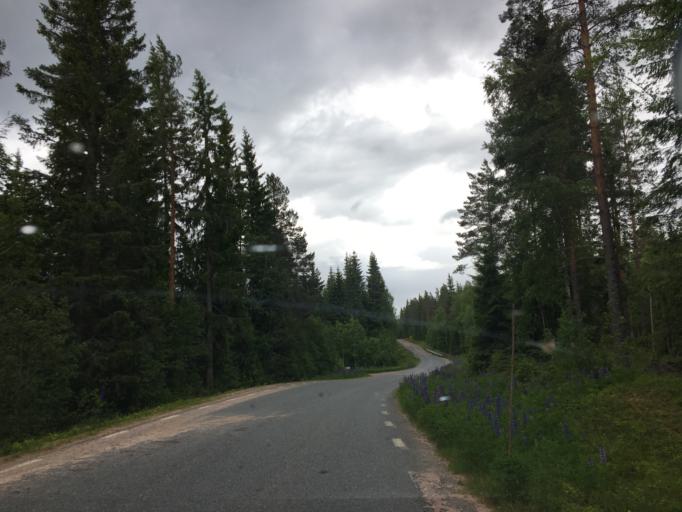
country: SE
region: Vaermland
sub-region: Filipstads Kommun
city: Lesjofors
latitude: 60.1156
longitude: 14.4643
